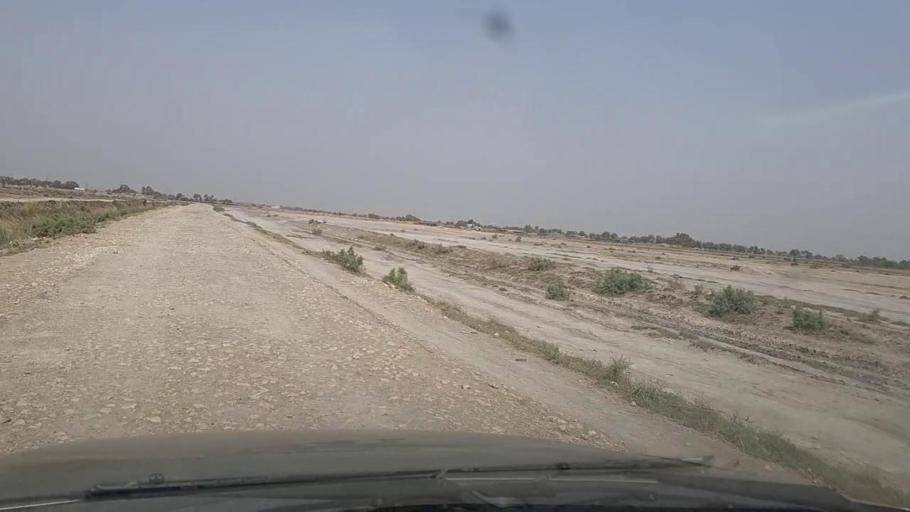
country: PK
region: Balochistan
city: Sohbatpur
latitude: 28.4126
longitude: 68.6942
